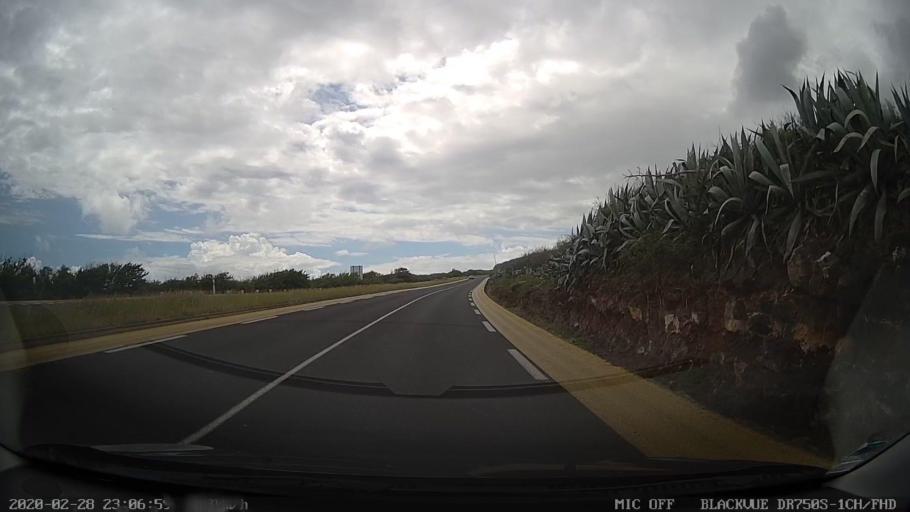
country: RE
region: Reunion
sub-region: Reunion
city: Saint-Leu
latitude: -21.1499
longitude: 55.2756
